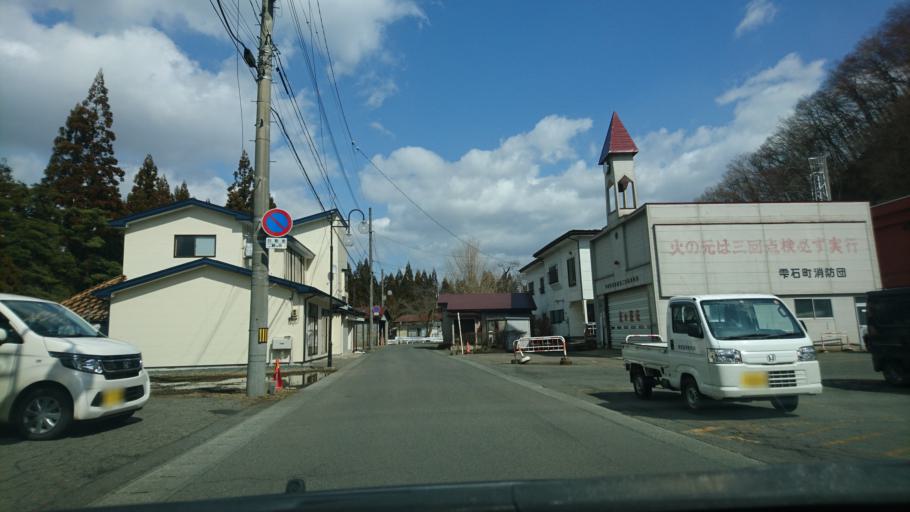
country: JP
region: Iwate
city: Shizukuishi
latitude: 39.6378
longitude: 140.9240
